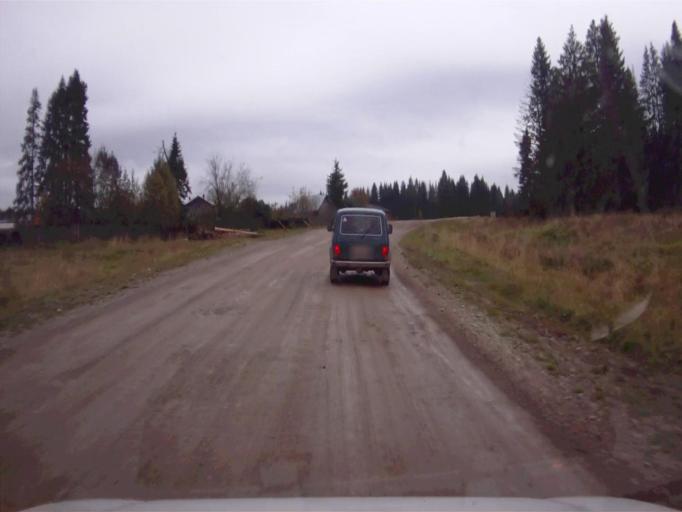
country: RU
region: Chelyabinsk
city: Nyazepetrovsk
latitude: 56.0617
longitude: 59.5643
